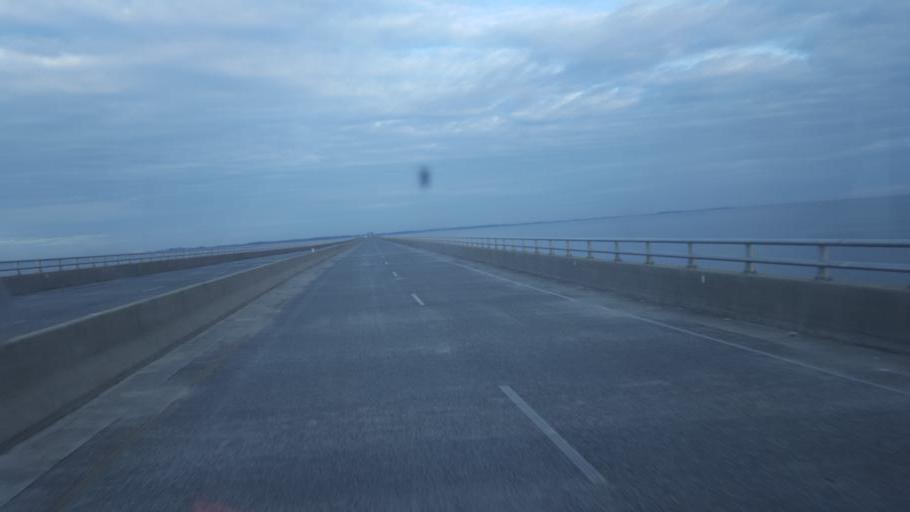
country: US
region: North Carolina
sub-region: Dare County
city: Manteo
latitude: 35.8821
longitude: -75.6844
